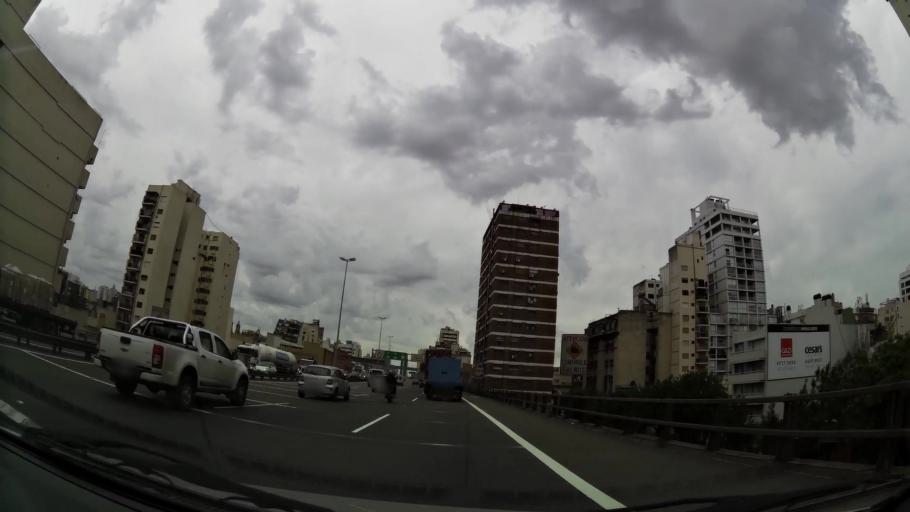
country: AR
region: Buenos Aires F.D.
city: Buenos Aires
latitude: -34.6230
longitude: -58.3753
